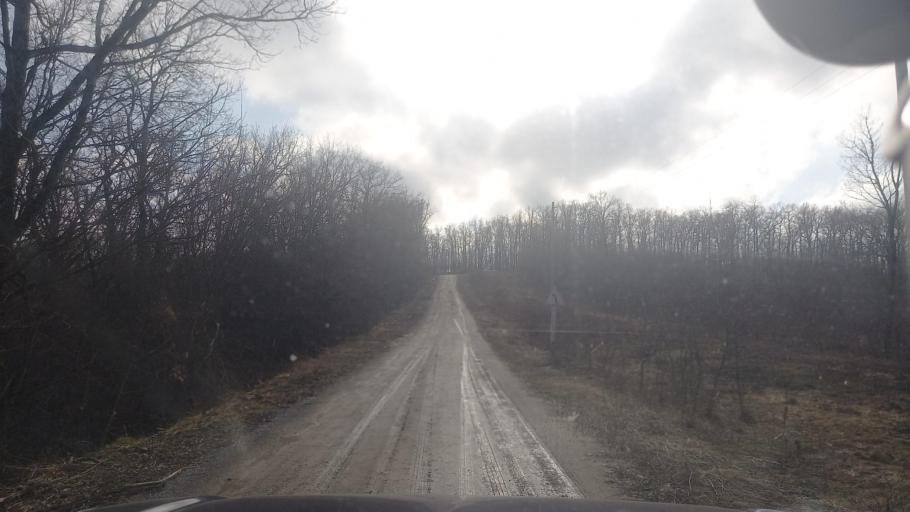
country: RU
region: Krasnodarskiy
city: Smolenskaya
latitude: 44.7431
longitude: 38.7762
